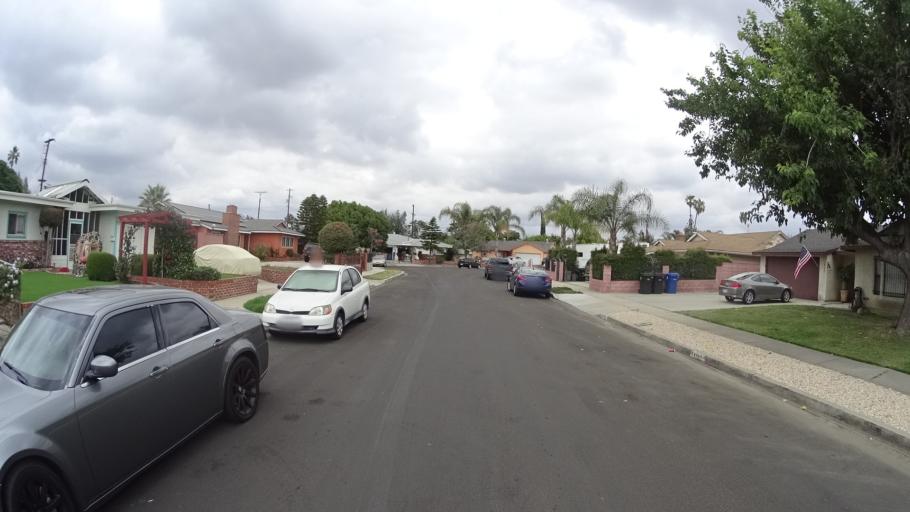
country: US
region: California
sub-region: Los Angeles County
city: San Fernando
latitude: 34.2530
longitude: -118.4432
